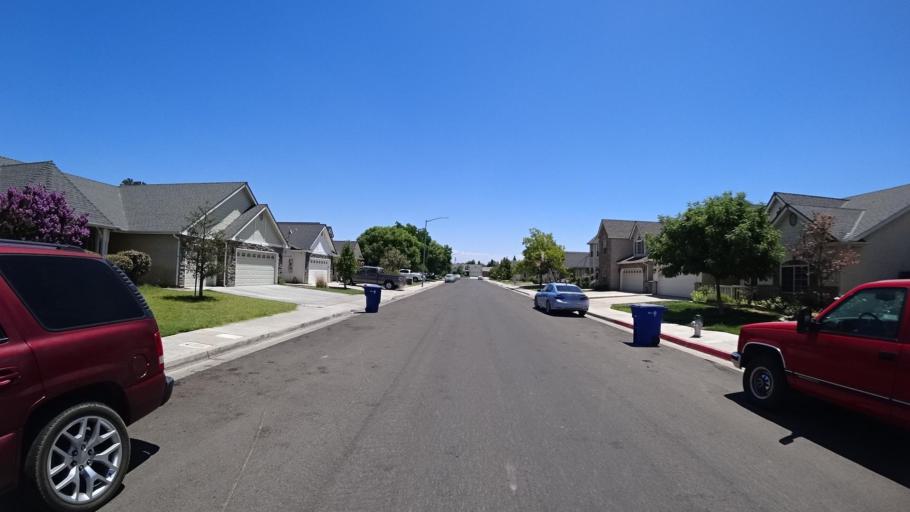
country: US
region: California
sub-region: Fresno County
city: Sunnyside
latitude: 36.7321
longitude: -119.6708
